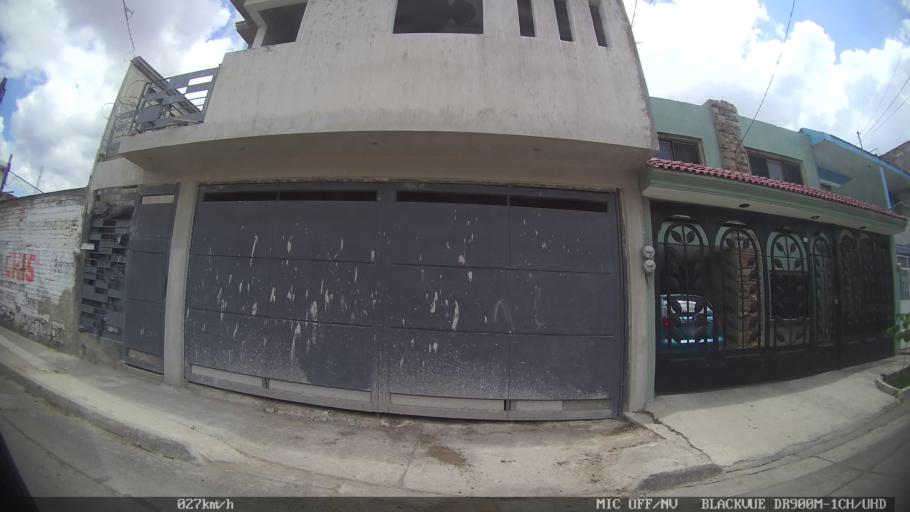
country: MX
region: Jalisco
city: Tlaquepaque
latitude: 20.6502
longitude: -103.2763
